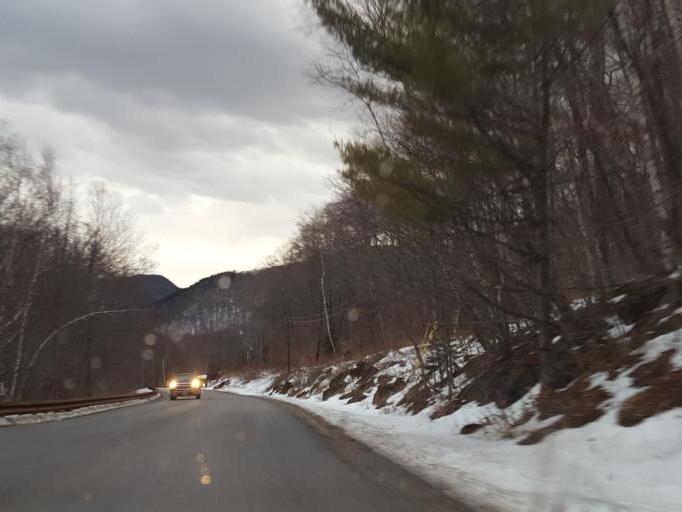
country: US
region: Vermont
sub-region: Rutland County
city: Rutland
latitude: 43.6150
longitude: -72.7677
